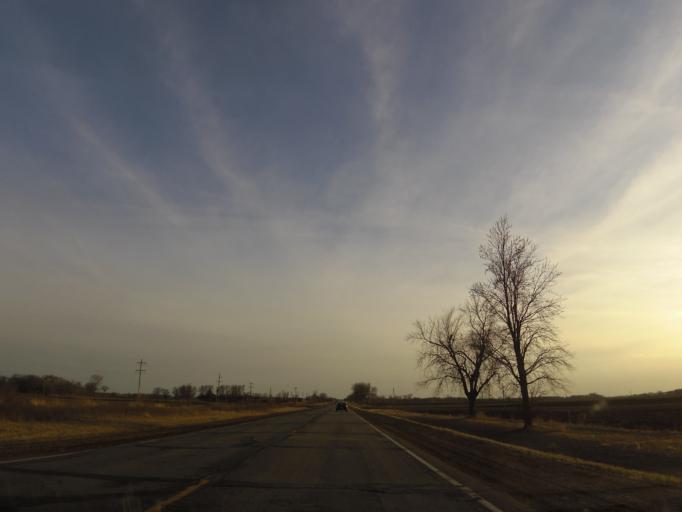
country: US
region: Minnesota
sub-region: Carver County
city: Norwood (historical)
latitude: 44.7047
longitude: -93.9888
